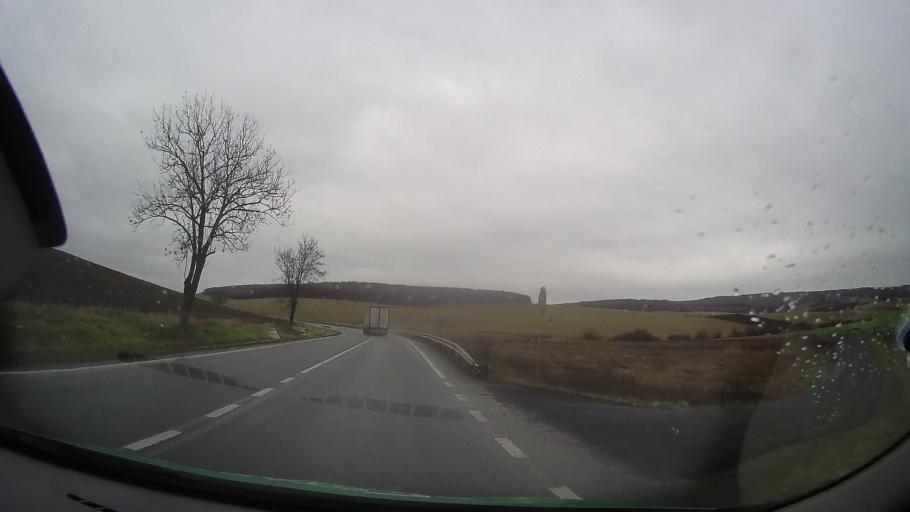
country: RO
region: Mures
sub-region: Comuna Lunca
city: Lunca
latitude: 46.8631
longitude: 24.5542
